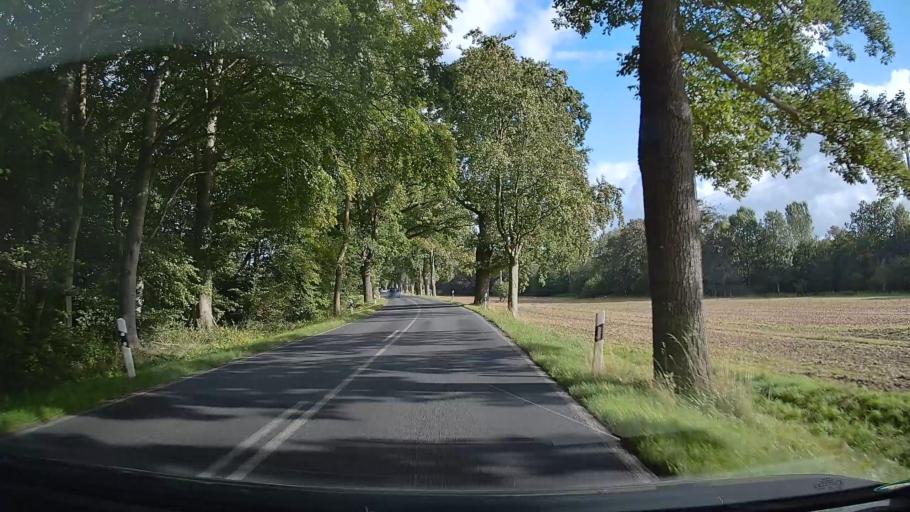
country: DE
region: Mecklenburg-Vorpommern
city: Putbus
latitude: 54.3839
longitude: 13.4752
